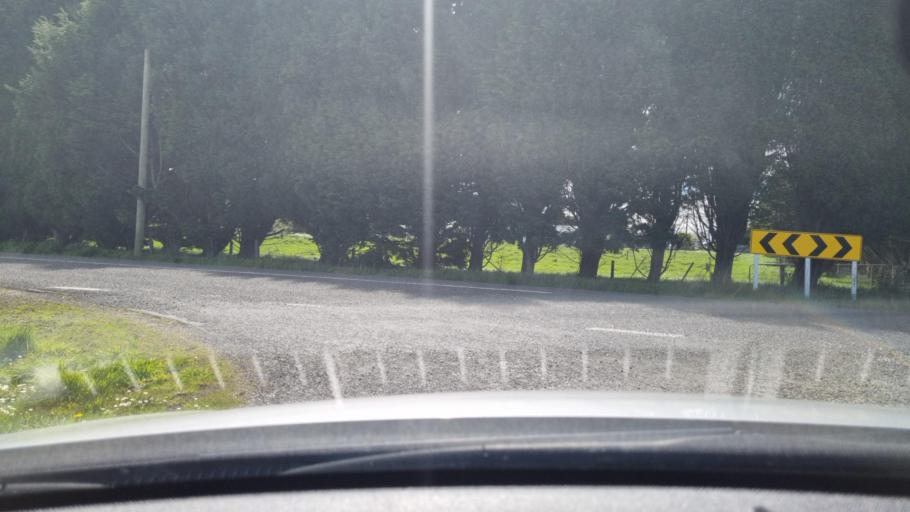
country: NZ
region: Southland
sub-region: Invercargill City
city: Invercargill
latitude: -46.4756
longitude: 168.3914
